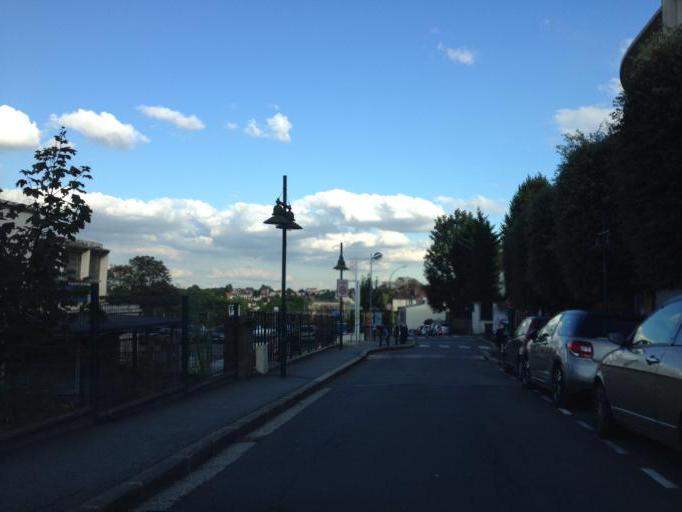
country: FR
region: Ile-de-France
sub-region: Departement des Hauts-de-Seine
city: Meudon
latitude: 48.8149
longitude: 2.2405
